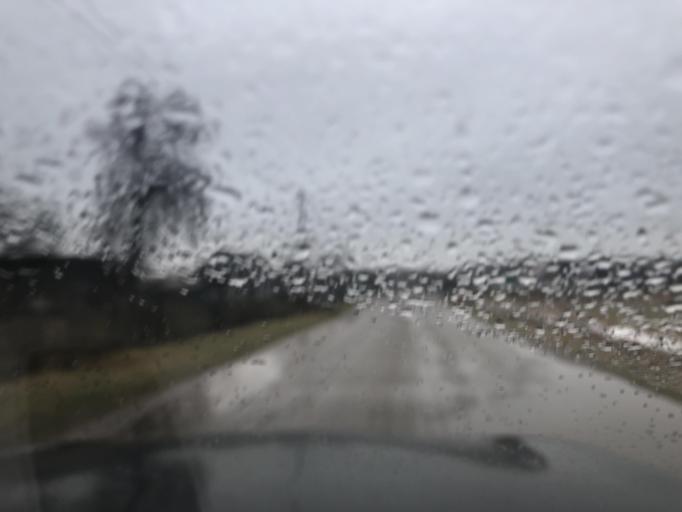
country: BY
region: Grodnenskaya
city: Hal'shany
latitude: 54.1637
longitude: 26.0880
